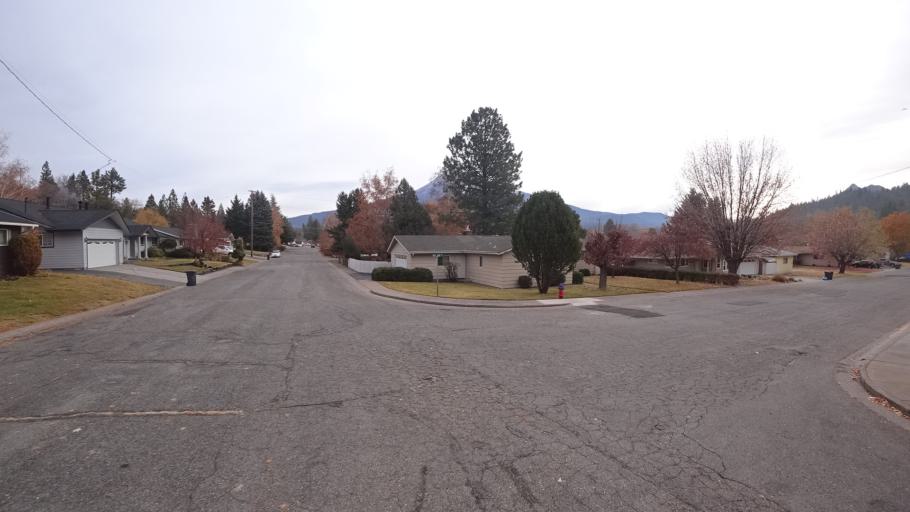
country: US
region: California
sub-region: Siskiyou County
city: Weed
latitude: 41.4170
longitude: -122.3910
